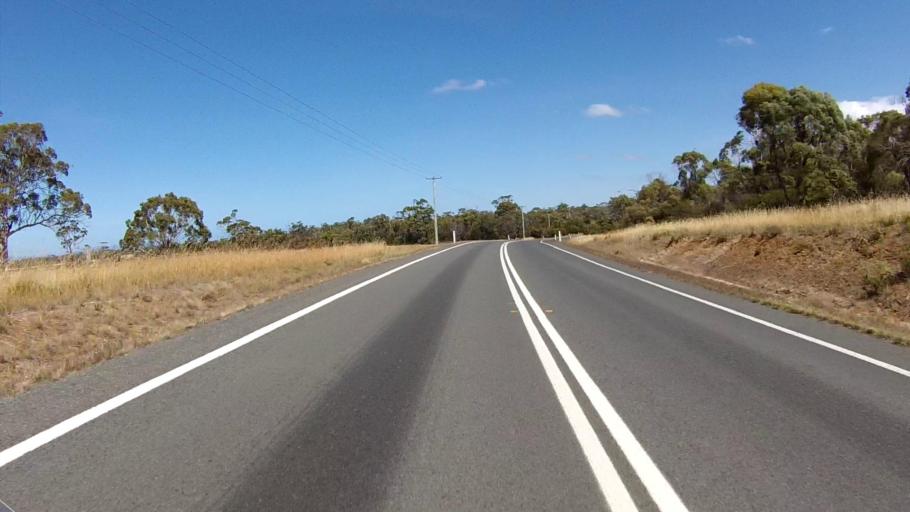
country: AU
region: Tasmania
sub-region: Break O'Day
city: St Helens
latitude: -42.0801
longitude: 148.0693
